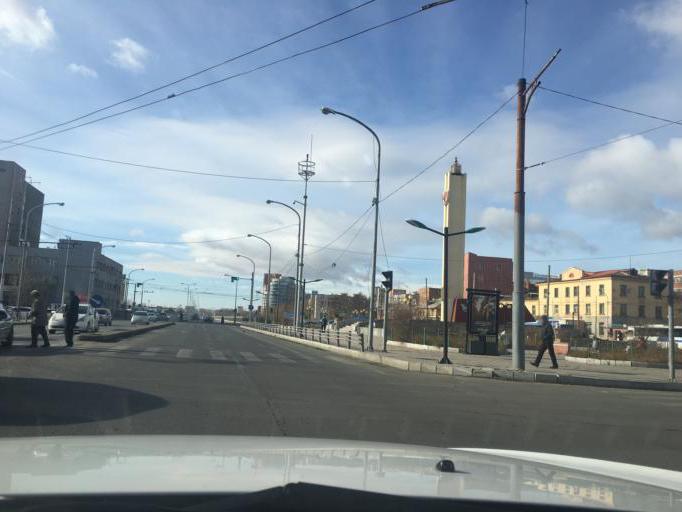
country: MN
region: Ulaanbaatar
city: Ulaanbaatar
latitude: 47.9092
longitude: 106.8848
